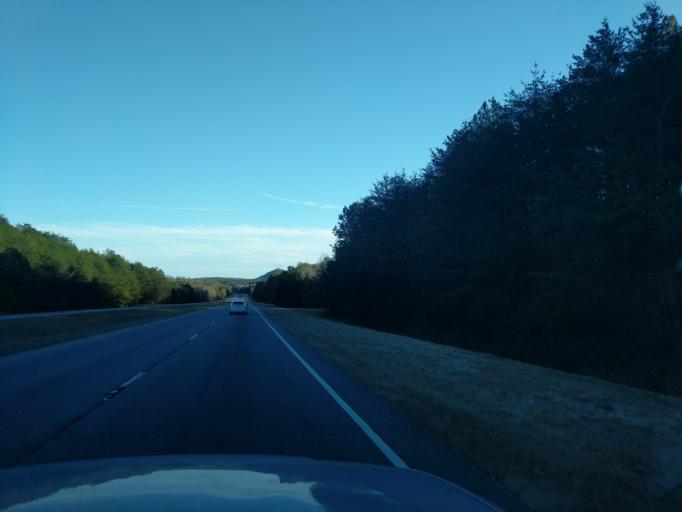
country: US
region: Georgia
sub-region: Stephens County
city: Toccoa
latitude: 34.5772
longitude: -83.4064
